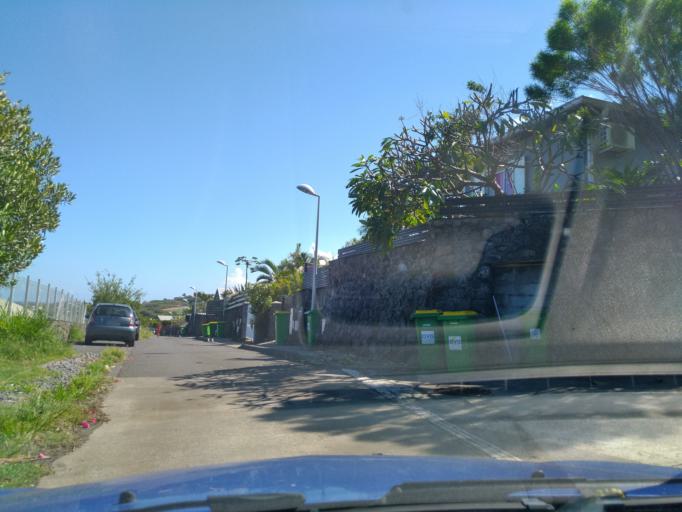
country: RE
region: Reunion
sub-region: Reunion
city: Petite-Ile
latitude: -21.3561
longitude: 55.5256
